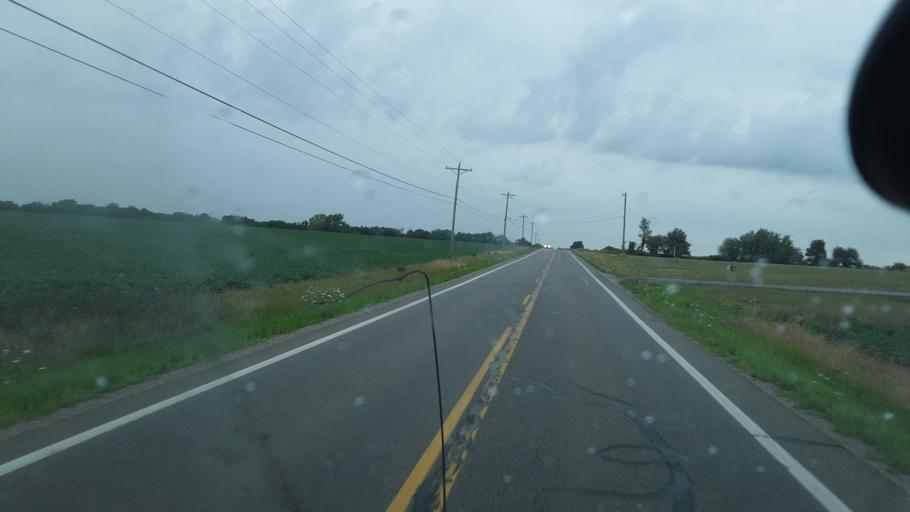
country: US
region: Ohio
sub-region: Williams County
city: Bryan
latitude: 41.4467
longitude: -84.6123
